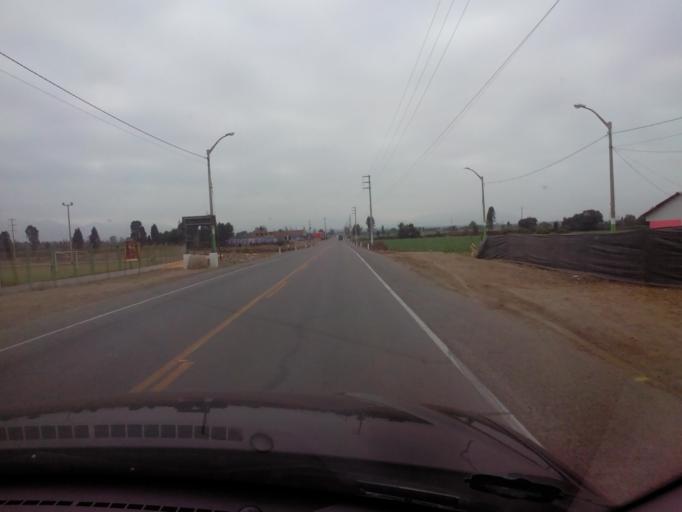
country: PE
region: Ica
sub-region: Provincia de Pisco
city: Independencia
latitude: -13.6832
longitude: -76.0642
